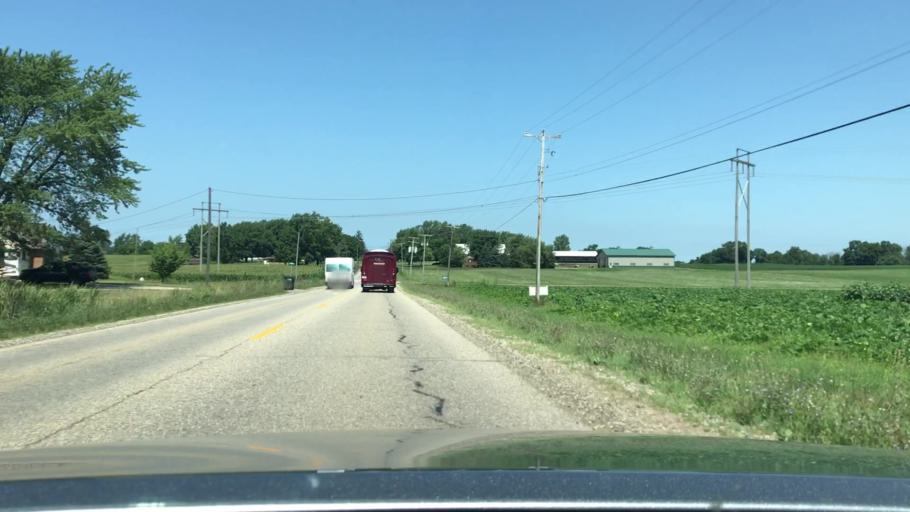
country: US
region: Michigan
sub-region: Ottawa County
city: Zeeland
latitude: 42.8768
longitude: -86.0800
